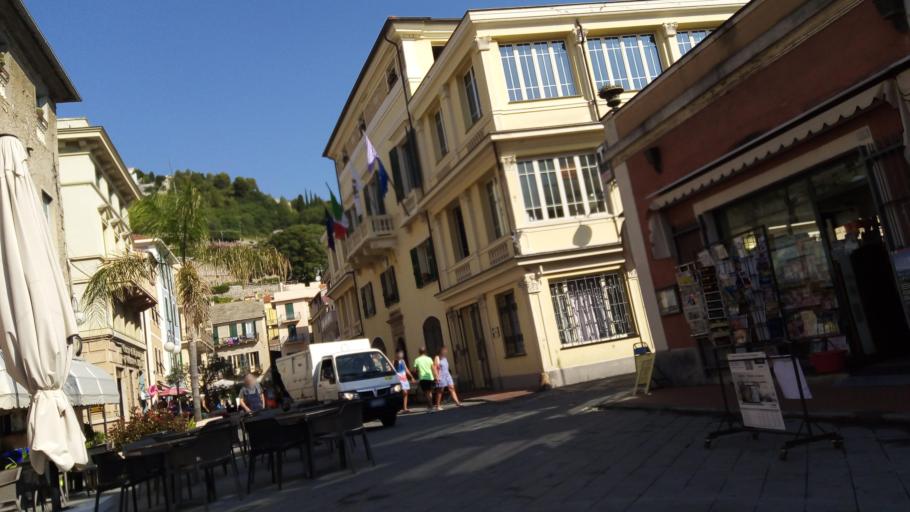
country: IT
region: Liguria
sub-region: Provincia di Savona
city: Pietra Ligure
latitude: 44.1485
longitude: 8.2829
